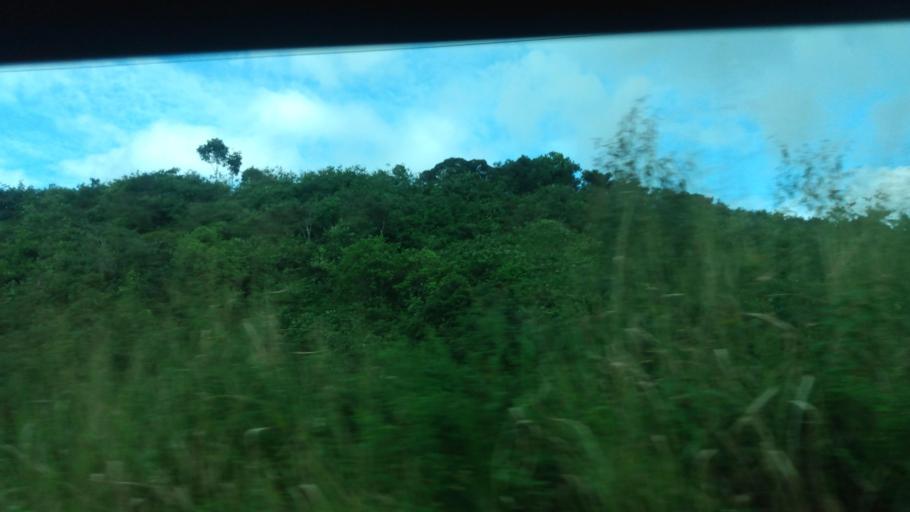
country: BR
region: Pernambuco
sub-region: Quipapa
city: Quipapa
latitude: -8.7896
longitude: -35.9788
